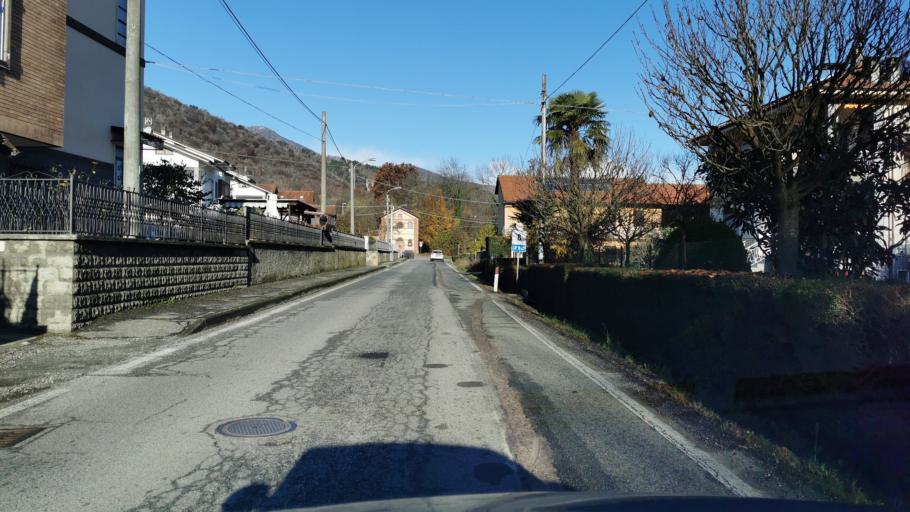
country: IT
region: Piedmont
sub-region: Provincia di Torino
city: La Cassa
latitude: 45.1773
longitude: 7.5173
